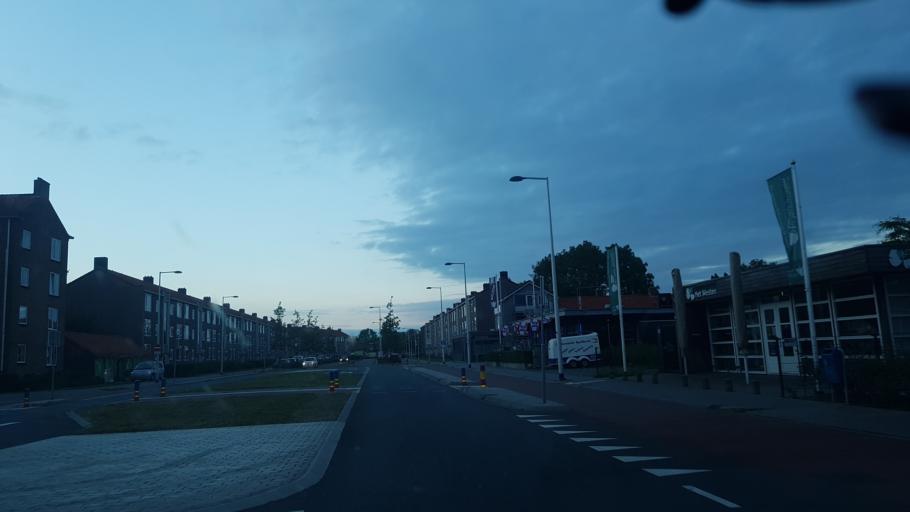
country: NL
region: Friesland
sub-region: Gemeente Leeuwarden
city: Bilgaard
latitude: 53.2080
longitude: 5.7780
